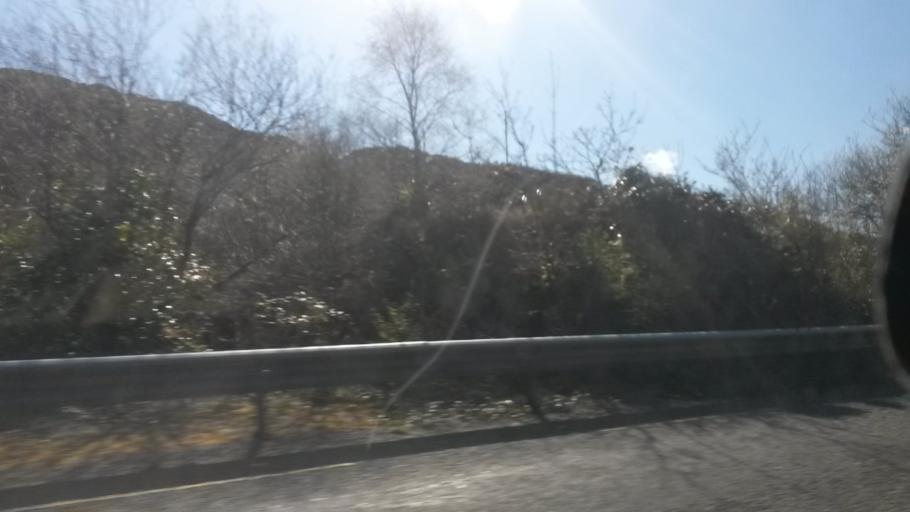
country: IE
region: Munster
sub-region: Ciarrai
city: Cill Airne
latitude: 51.9234
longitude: -9.3844
